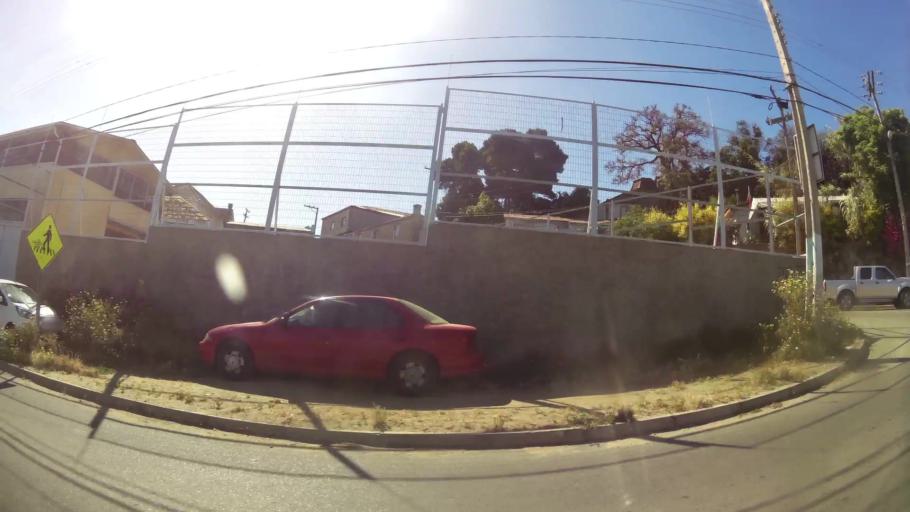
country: CL
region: Valparaiso
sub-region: Provincia de Valparaiso
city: Valparaiso
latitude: -33.0614
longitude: -71.5941
